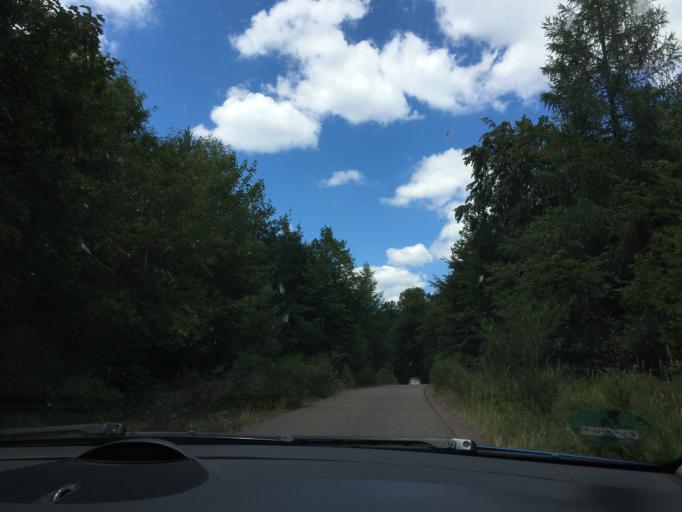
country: DE
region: Rheinland-Pfalz
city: Leimen
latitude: 49.2595
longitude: 7.8287
